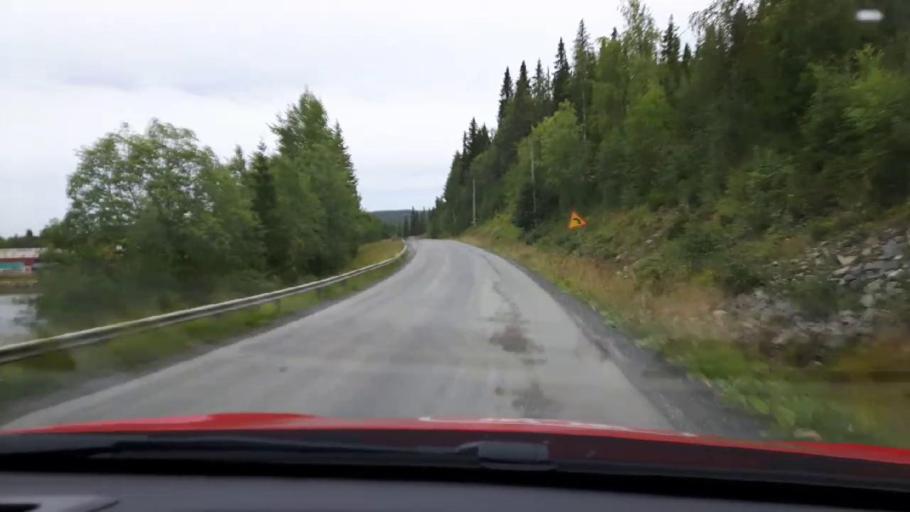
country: SE
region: Jaemtland
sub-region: Are Kommun
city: Jarpen
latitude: 63.4087
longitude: 13.3578
